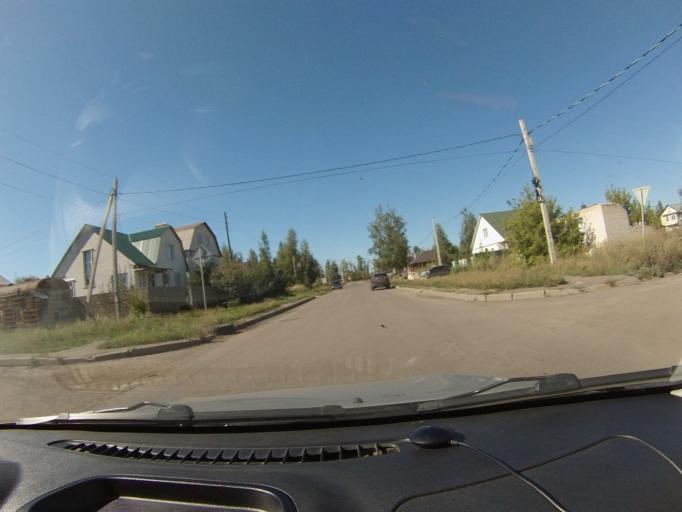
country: RU
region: Tambov
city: Komsomolets
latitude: 52.7674
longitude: 41.3658
